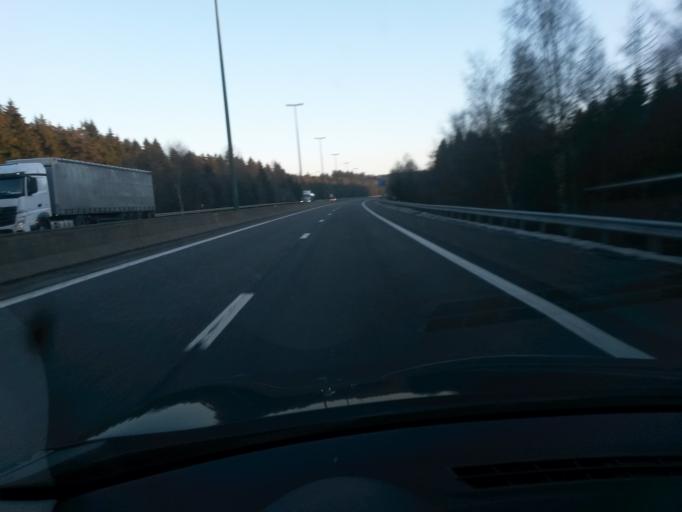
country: BE
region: Wallonia
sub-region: Province de Liege
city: Waimes
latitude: 50.3462
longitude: 6.0814
